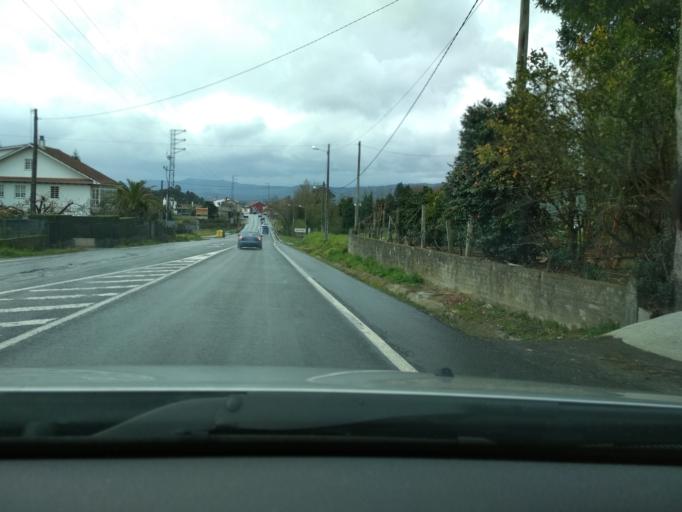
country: ES
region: Galicia
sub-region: Provincia da Coruna
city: Santiago de Compostela
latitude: 42.8316
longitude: -8.5945
